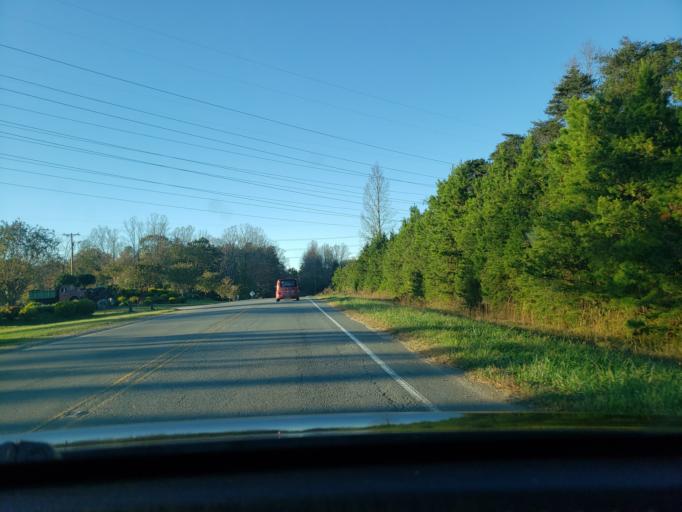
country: US
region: North Carolina
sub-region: Forsyth County
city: Walkertown
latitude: 36.1962
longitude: -80.1642
